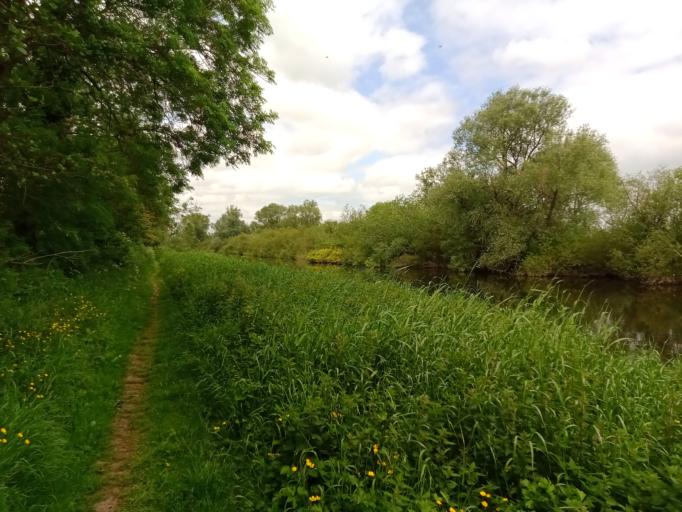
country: IE
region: Leinster
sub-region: County Carlow
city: Carlow
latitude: 52.7971
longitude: -6.9617
